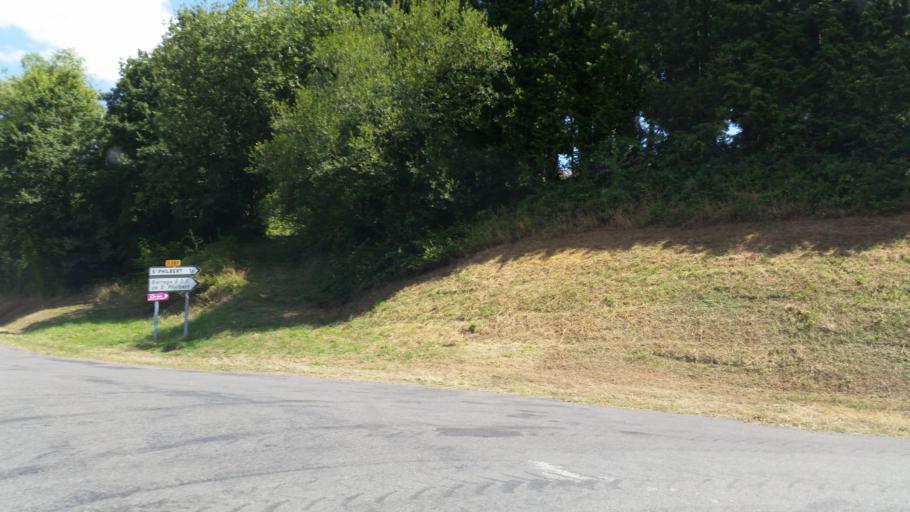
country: FR
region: Lower Normandy
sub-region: Departement du Calvados
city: Clecy
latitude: 48.8521
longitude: -0.3800
